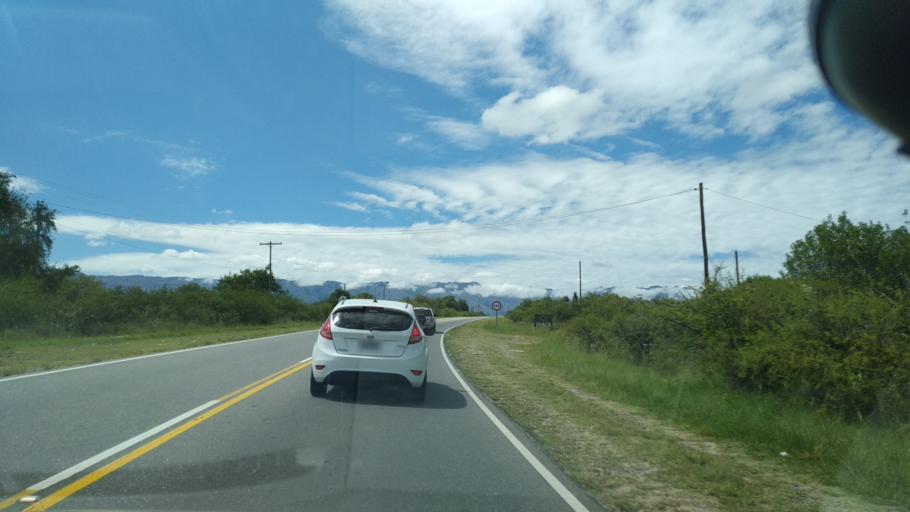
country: AR
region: Cordoba
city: Mina Clavero
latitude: -31.7593
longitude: -64.9722
